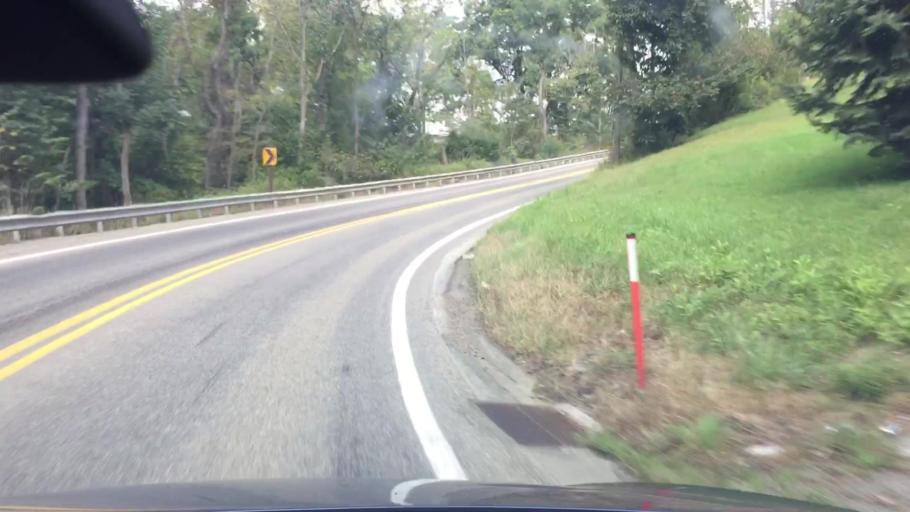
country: US
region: Pennsylvania
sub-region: Allegheny County
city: Cheswick
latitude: 40.5604
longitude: -79.8204
